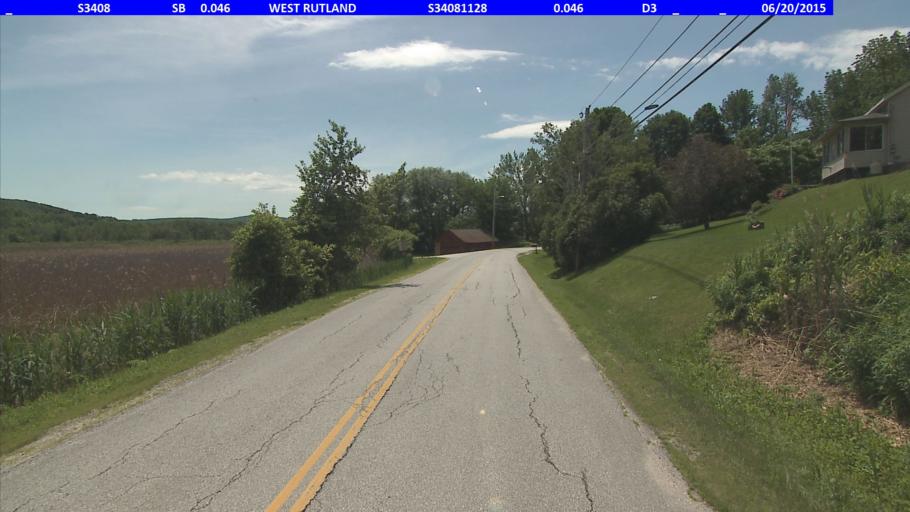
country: US
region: Vermont
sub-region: Rutland County
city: West Rutland
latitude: 43.6110
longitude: -73.0625
